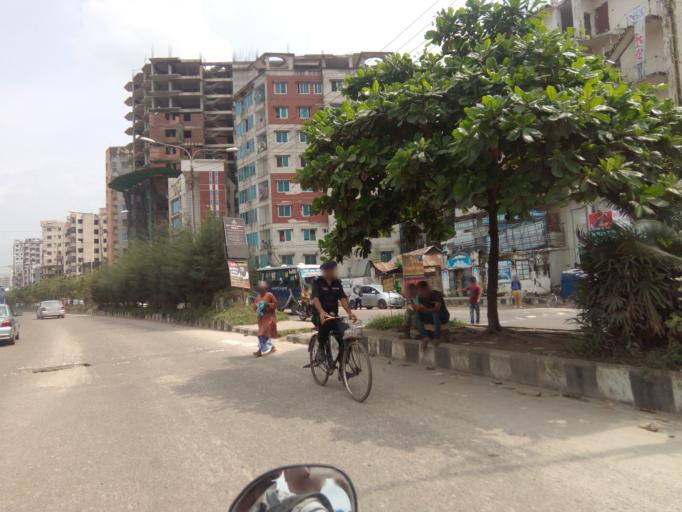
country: BD
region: Dhaka
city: Tungi
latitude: 23.8224
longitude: 90.3936
